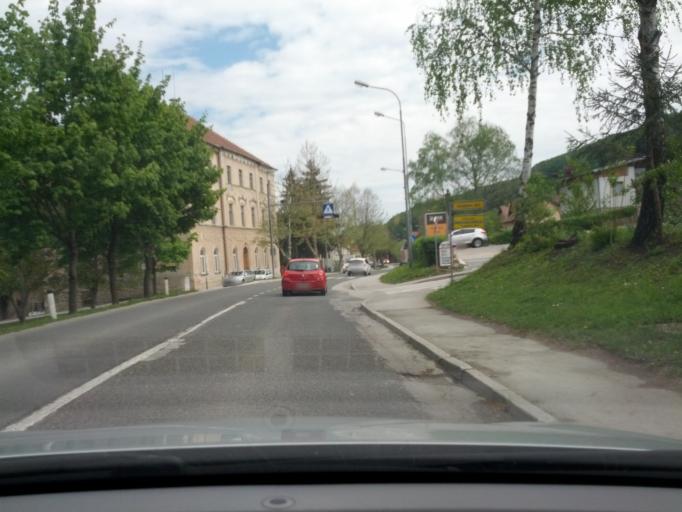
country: SI
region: Smarje pri Jelsah
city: Smarje pri Jelsah
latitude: 46.2294
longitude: 15.5137
